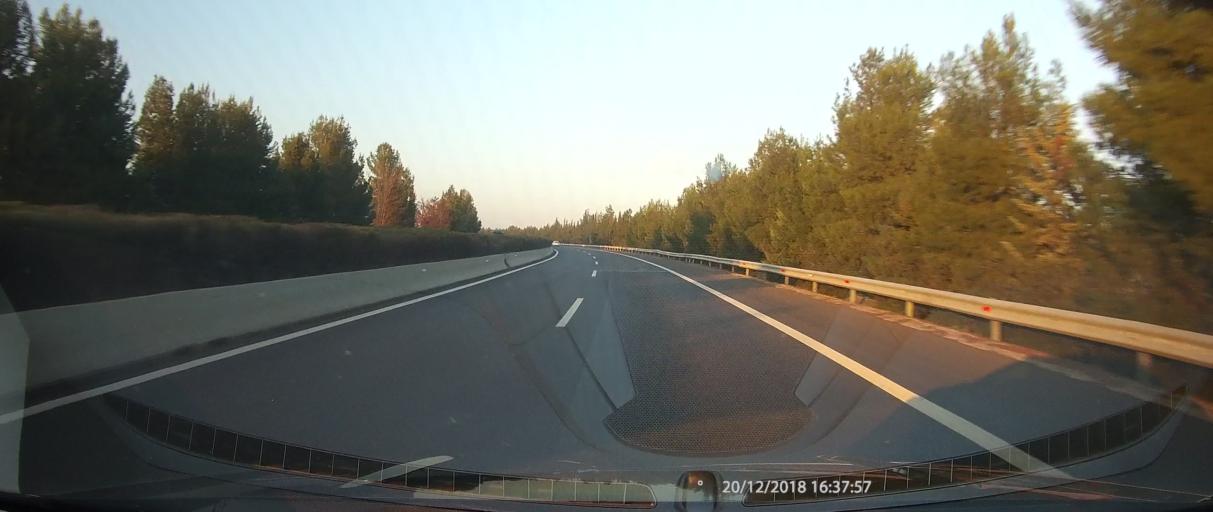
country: GR
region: Thessaly
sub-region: Nomos Magnisias
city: Velestino
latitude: 39.3367
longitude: 22.7833
